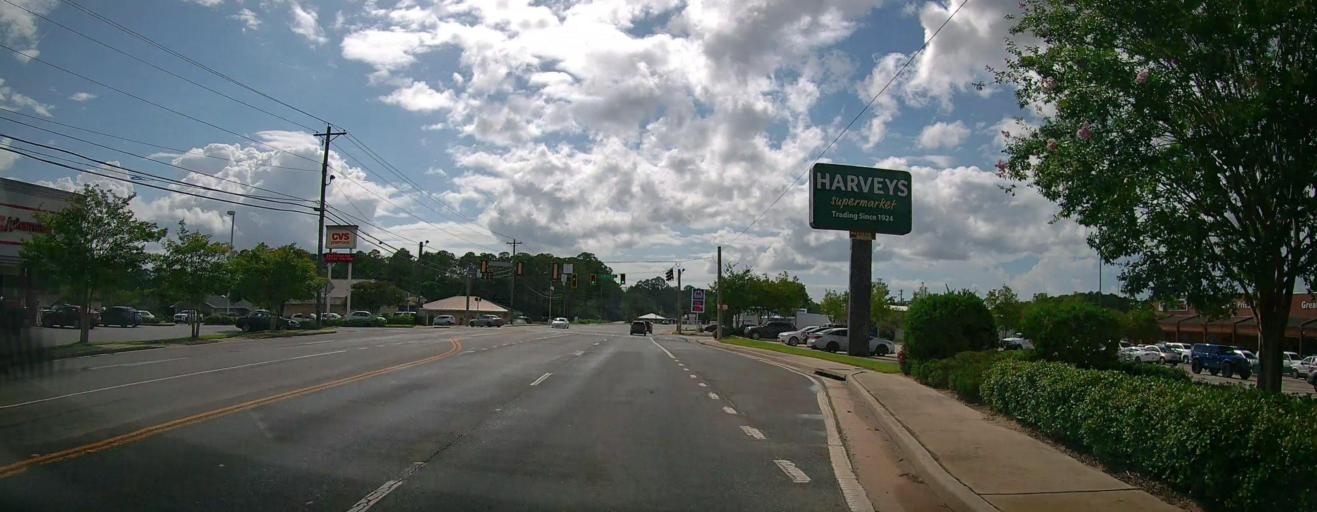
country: US
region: Georgia
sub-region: Coffee County
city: Douglas
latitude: 31.5093
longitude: -82.8603
